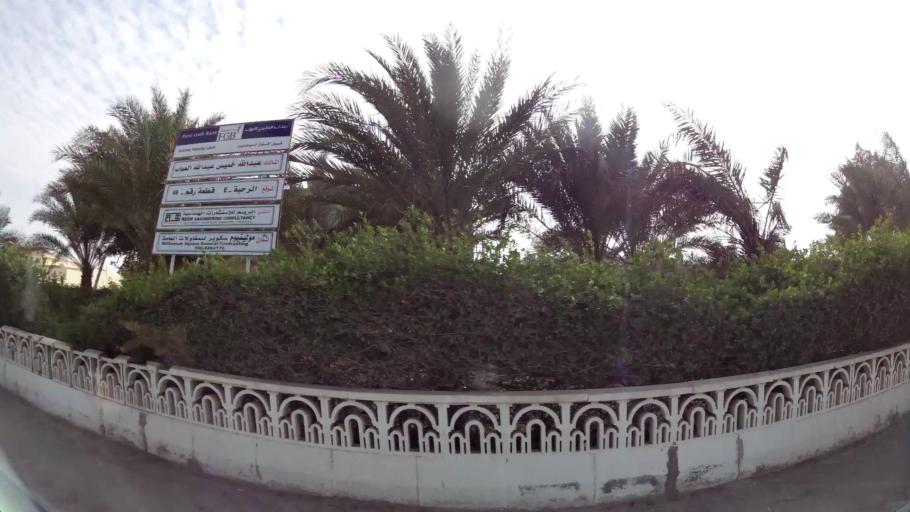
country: AE
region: Abu Dhabi
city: Abu Dhabi
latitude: 24.5910
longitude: 54.6952
